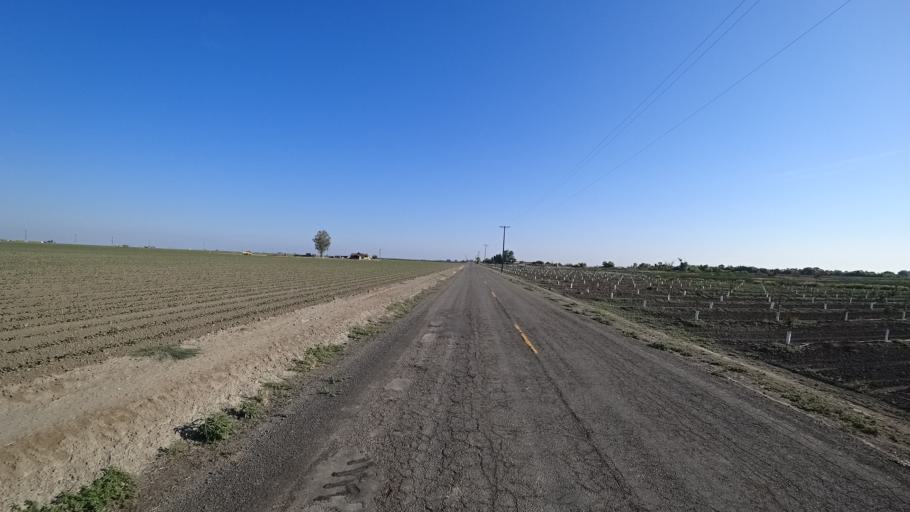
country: US
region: California
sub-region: Fresno County
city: Riverdale
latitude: 36.3848
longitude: -119.9278
